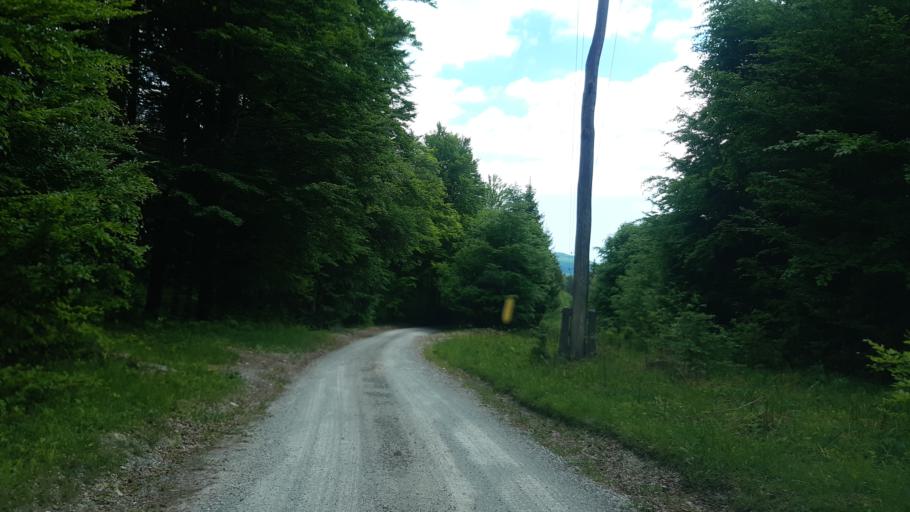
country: SI
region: Dolenjske Toplice
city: Dolenjske Toplice
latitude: 45.6176
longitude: 15.0134
